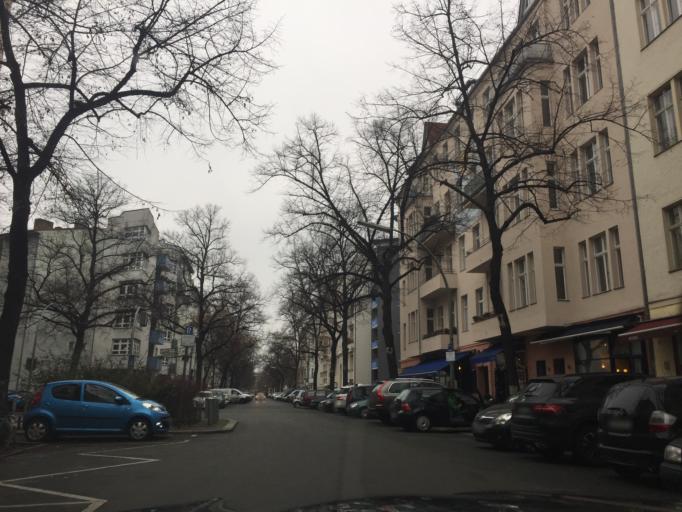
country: DE
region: Berlin
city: Hansaviertel
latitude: 52.5071
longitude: 13.3215
